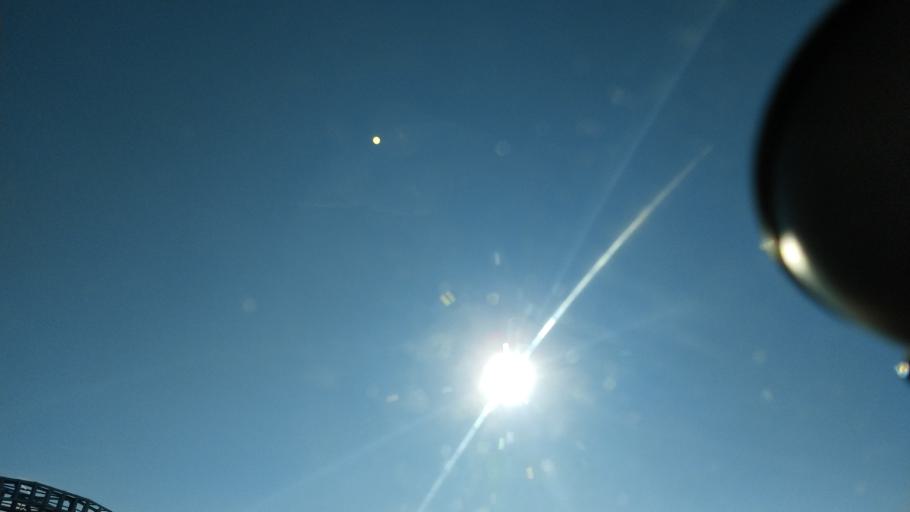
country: RO
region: Iasi
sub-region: Comuna Butea
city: Butea
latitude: 47.0851
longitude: 26.9015
